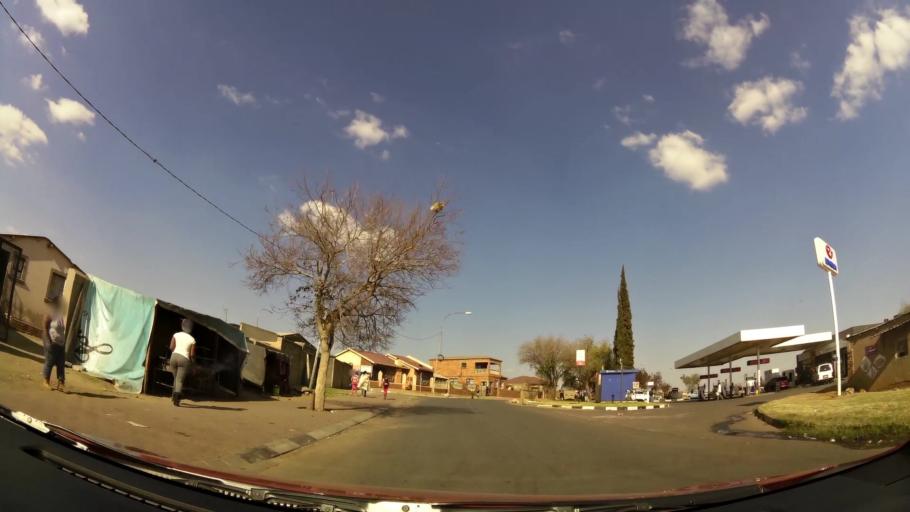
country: ZA
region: Gauteng
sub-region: City of Johannesburg Metropolitan Municipality
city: Roodepoort
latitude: -26.2134
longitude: 27.8862
